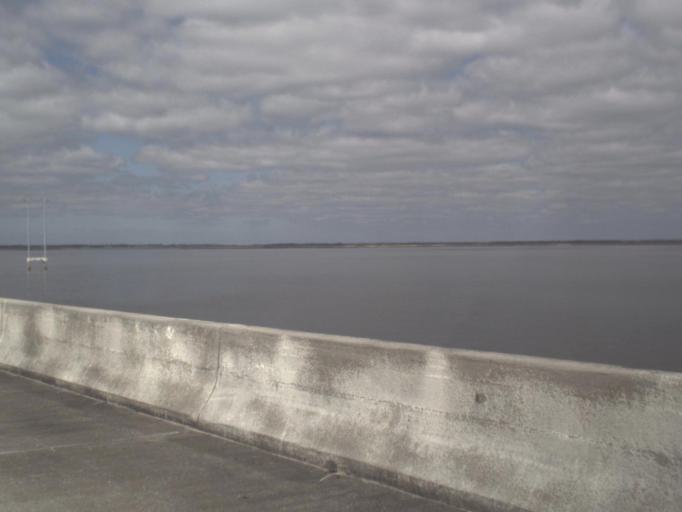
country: US
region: Florida
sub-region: Franklin County
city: Apalachicola
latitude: 29.7303
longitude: -84.9385
